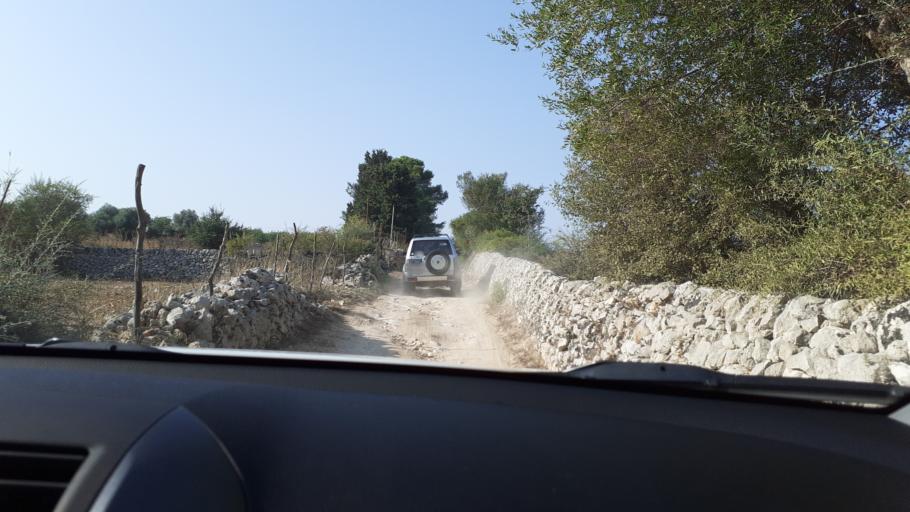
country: IT
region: Sicily
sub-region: Provincia di Siracusa
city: Canicattini Bagni
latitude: 36.9829
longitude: 15.0926
